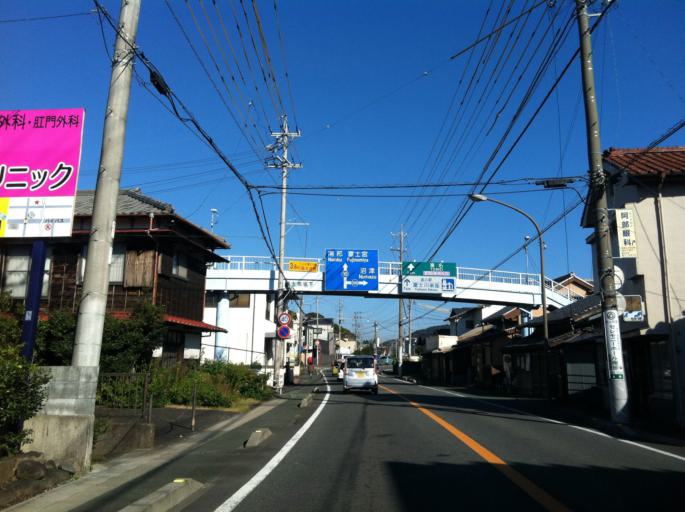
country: JP
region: Shizuoka
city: Fuji
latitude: 35.1534
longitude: 138.6213
